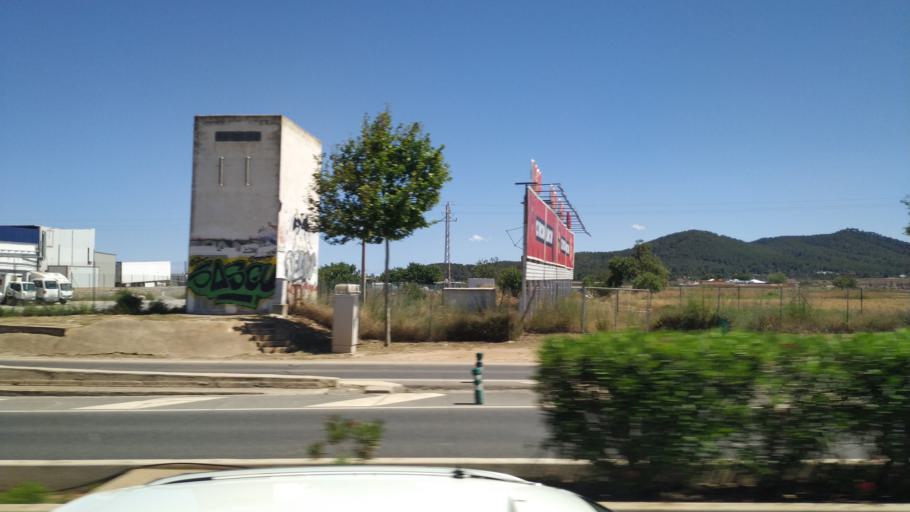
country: ES
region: Balearic Islands
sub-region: Illes Balears
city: Ibiza
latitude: 38.8848
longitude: 1.3906
